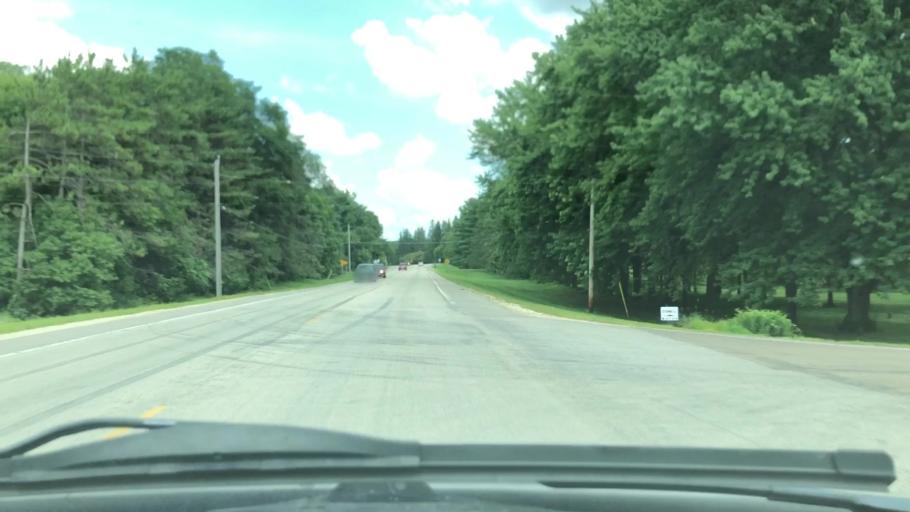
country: US
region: Minnesota
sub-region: Olmsted County
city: Rochester
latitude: 43.9881
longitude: -92.5036
